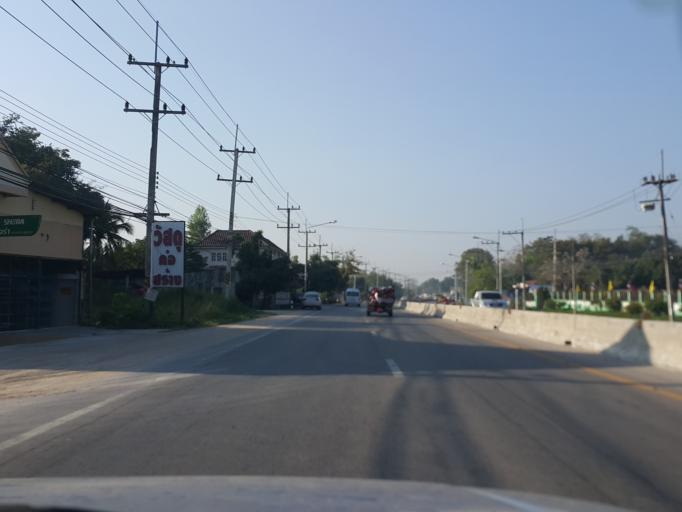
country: TH
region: Chiang Mai
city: San Pa Tong
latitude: 18.6069
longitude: 98.8926
